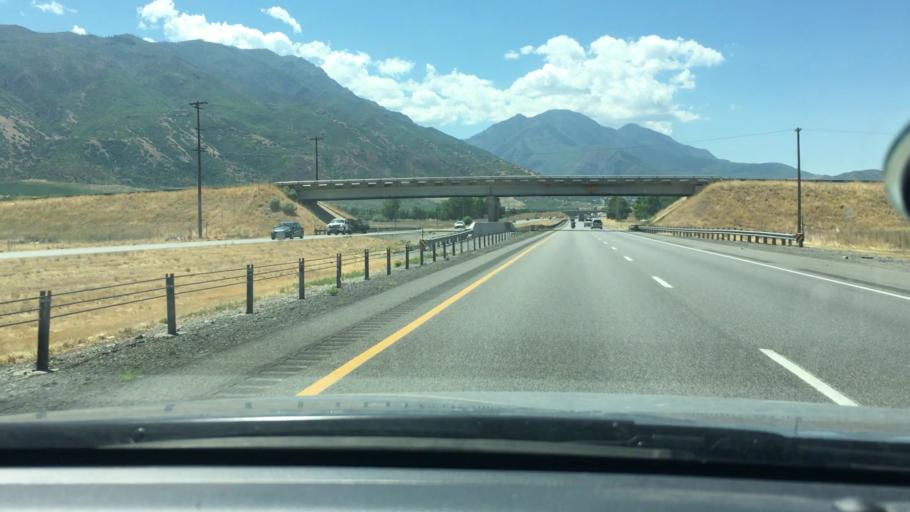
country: US
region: Utah
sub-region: Utah County
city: Payson
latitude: 40.0131
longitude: -111.7626
